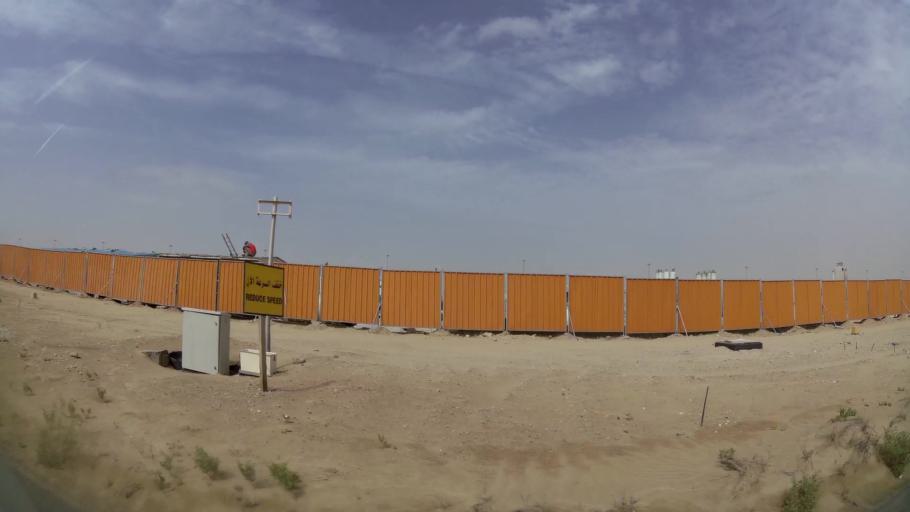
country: AE
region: Abu Dhabi
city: Abu Dhabi
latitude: 24.3357
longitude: 54.5059
